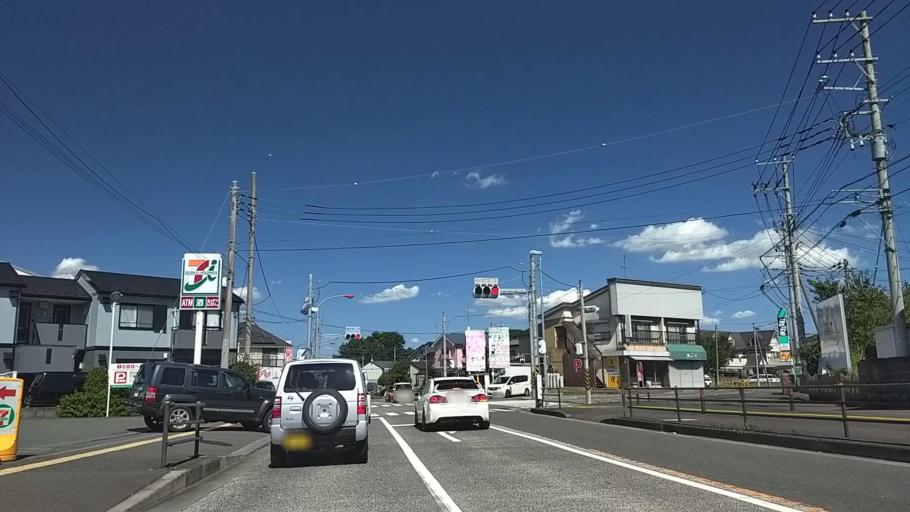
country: JP
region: Tokyo
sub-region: Machida-shi
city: Machida
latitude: 35.5739
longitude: 139.4061
